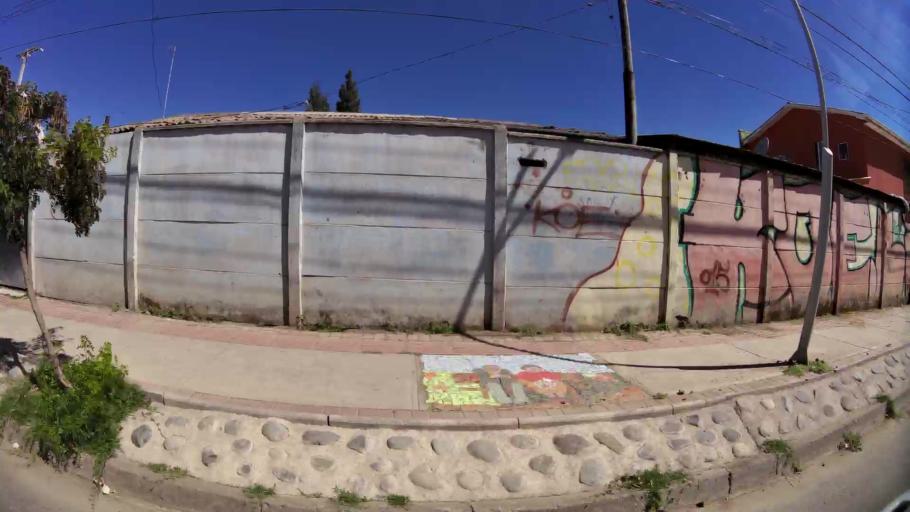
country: CL
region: O'Higgins
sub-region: Provincia de Cachapoal
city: Rancagua
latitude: -34.1696
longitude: -70.7081
